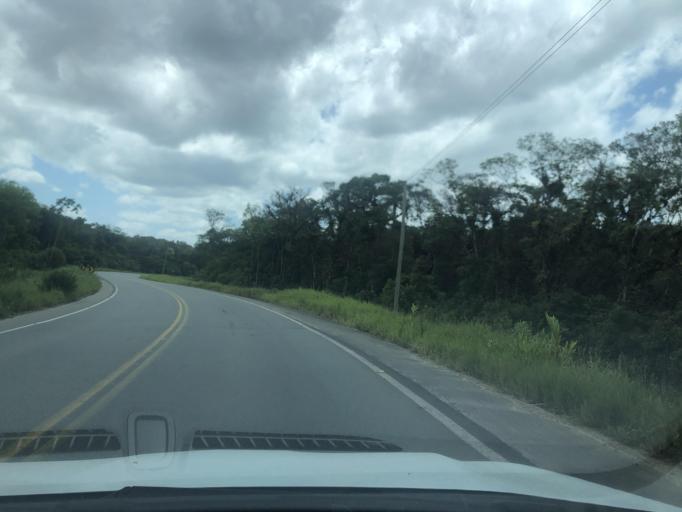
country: BR
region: Santa Catarina
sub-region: Joinville
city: Joinville
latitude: -26.3970
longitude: -48.7613
